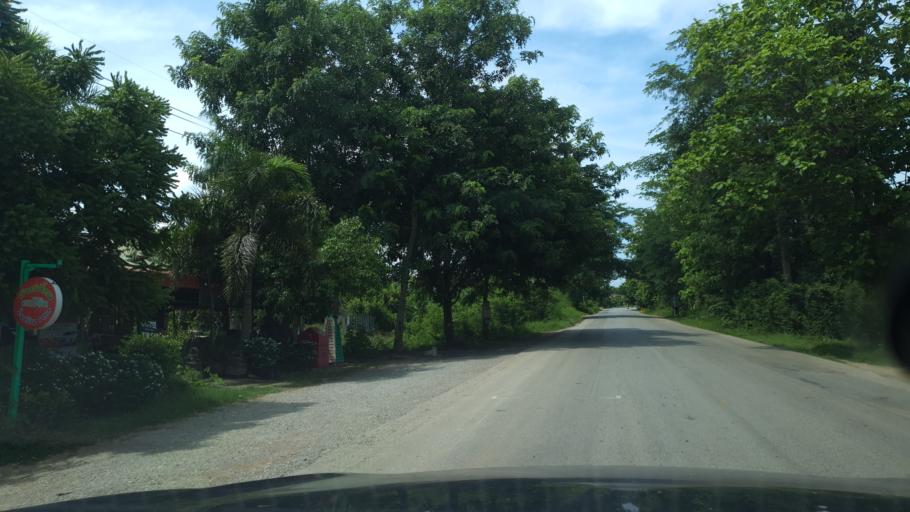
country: TH
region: Sukhothai
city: Sukhothai
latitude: 17.0645
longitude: 99.8299
